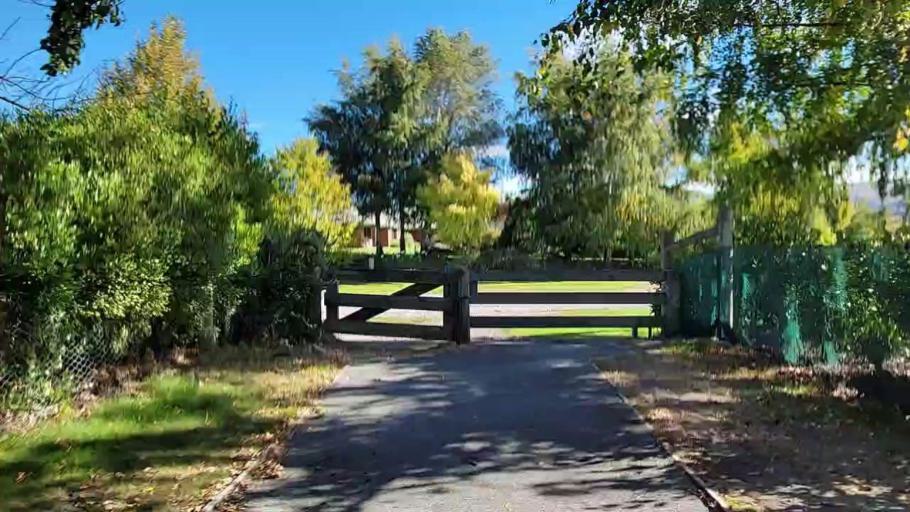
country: NZ
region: Otago
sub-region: Queenstown-Lakes District
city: Wanaka
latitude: -45.0323
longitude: 169.2093
